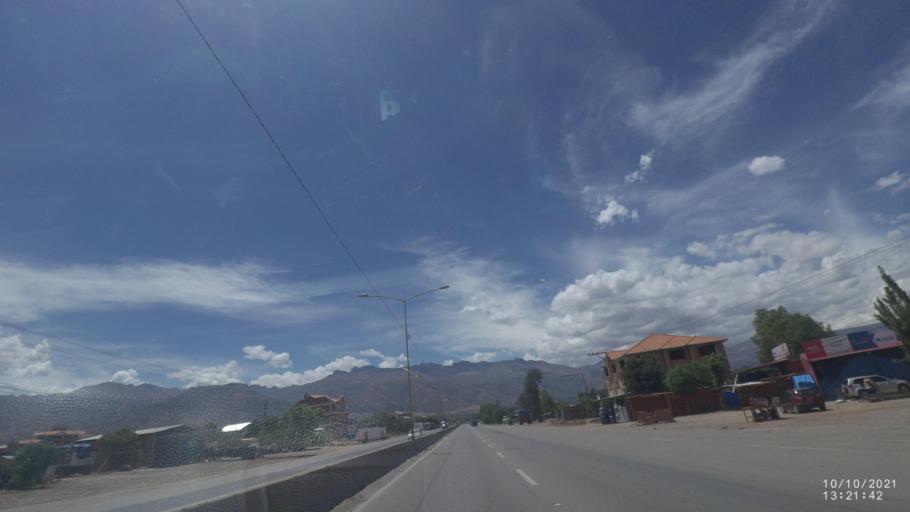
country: BO
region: Cochabamba
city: Sipe Sipe
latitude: -17.4234
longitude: -66.3318
